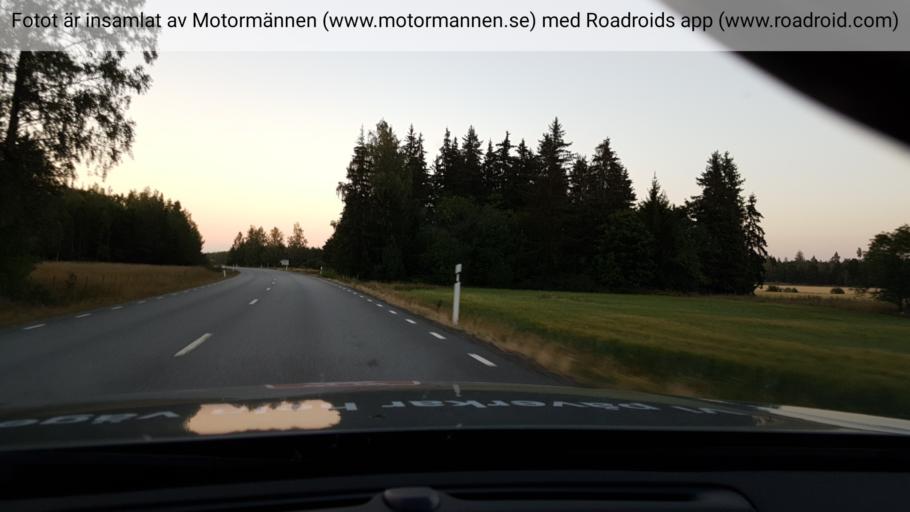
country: SE
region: Uppsala
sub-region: Heby Kommun
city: OEstervala
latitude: 60.1549
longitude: 17.2038
